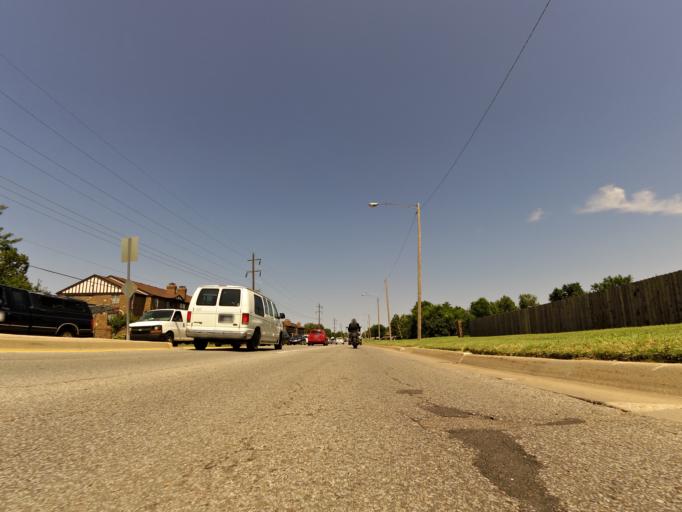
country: US
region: Kansas
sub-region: Sedgwick County
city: Bellaire
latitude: 37.7247
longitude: -97.2623
